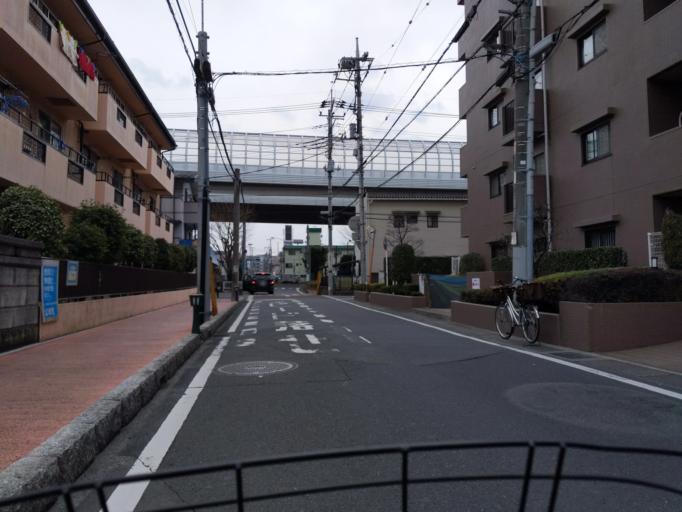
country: JP
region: Saitama
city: Soka
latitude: 35.8504
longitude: 139.7952
